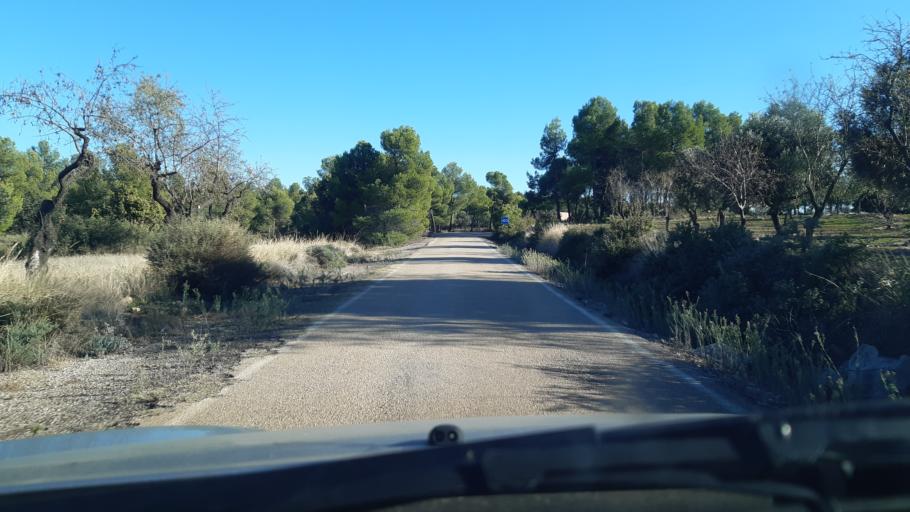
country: ES
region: Aragon
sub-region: Provincia de Teruel
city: Fornoles
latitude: 40.9129
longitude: -0.0186
